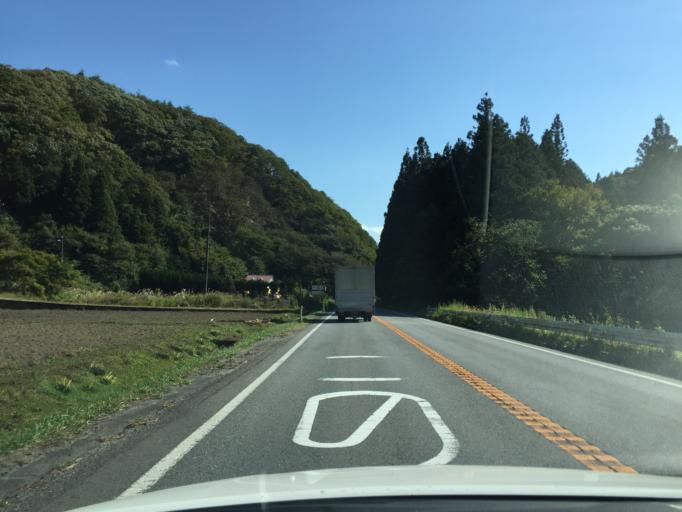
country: JP
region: Fukushima
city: Iwaki
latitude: 37.0804
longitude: 140.7830
